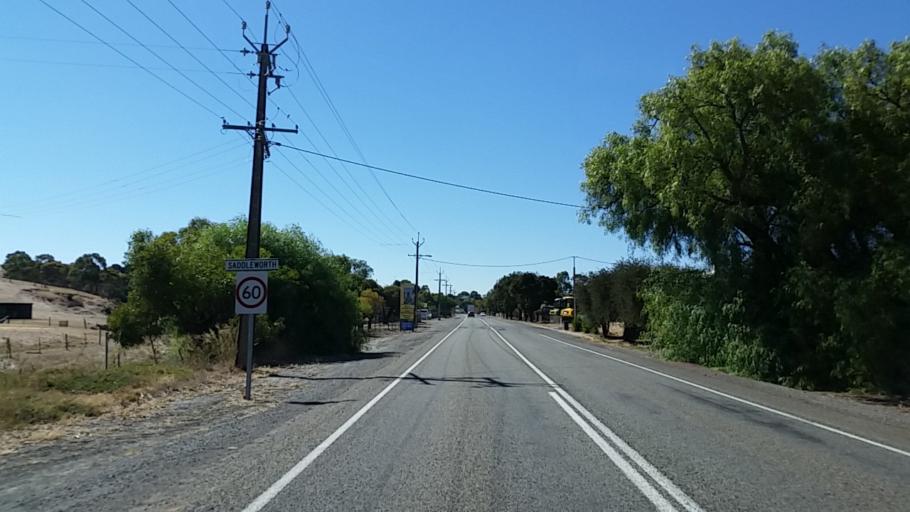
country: AU
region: South Australia
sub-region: Light
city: Kapunda
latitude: -34.0874
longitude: 138.7766
